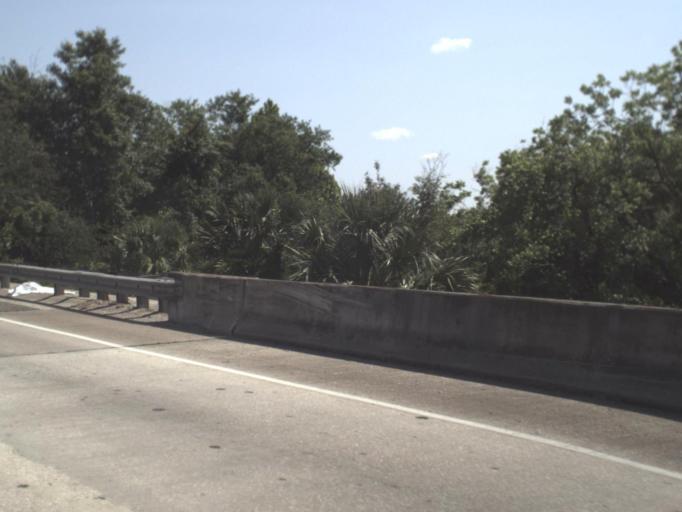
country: US
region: Florida
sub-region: Duval County
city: Jacksonville
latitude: 30.3517
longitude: -81.6683
